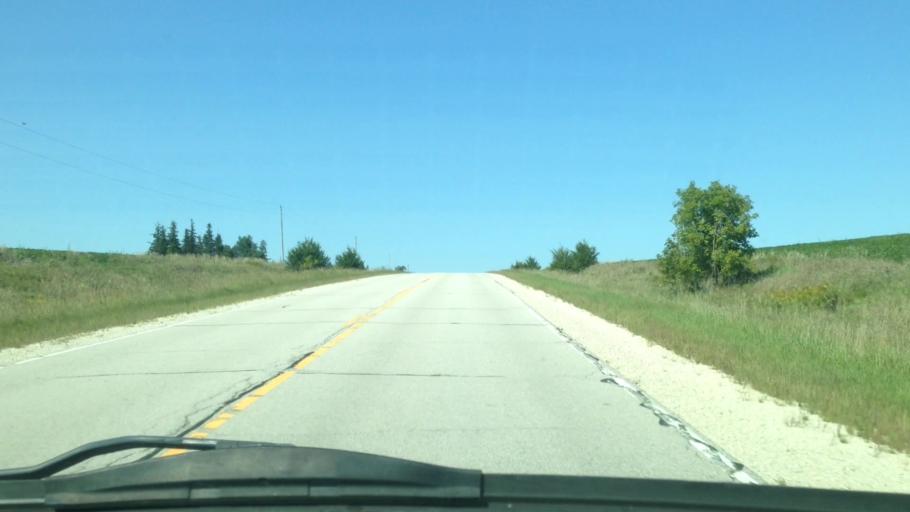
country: US
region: Minnesota
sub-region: Houston County
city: Spring Grove
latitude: 43.6352
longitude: -91.7903
